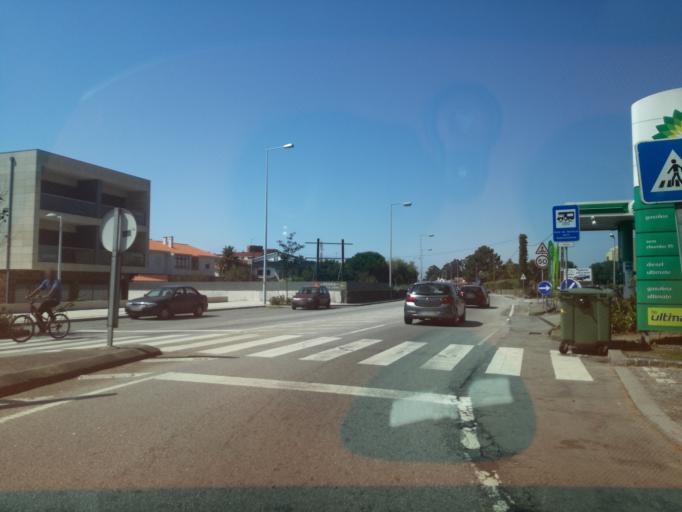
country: PT
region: Braga
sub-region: Esposende
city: Esposende
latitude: 41.5316
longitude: -8.7759
